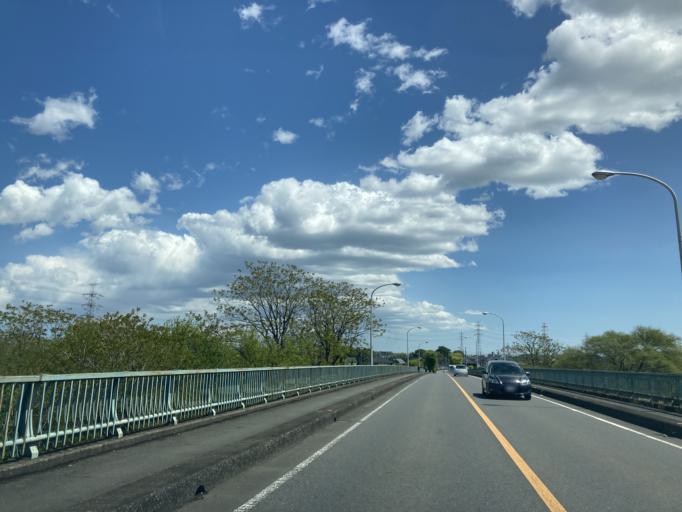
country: JP
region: Saitama
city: Sayama
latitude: 35.8751
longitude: 139.4124
